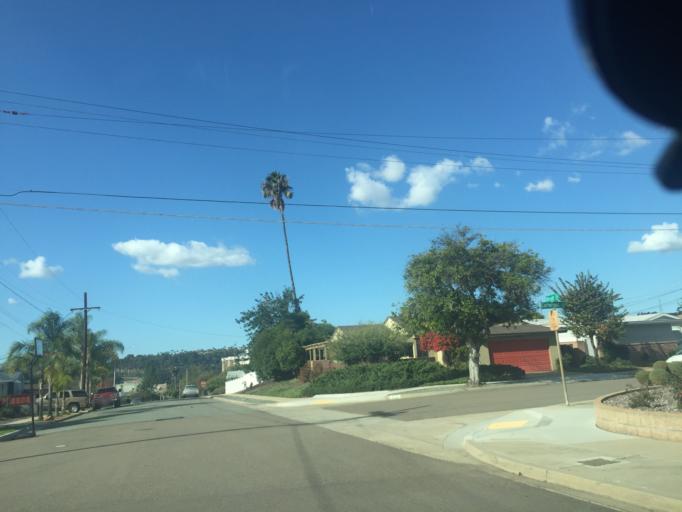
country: US
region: California
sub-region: San Diego County
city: La Mesa
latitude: 32.7908
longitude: -117.0907
